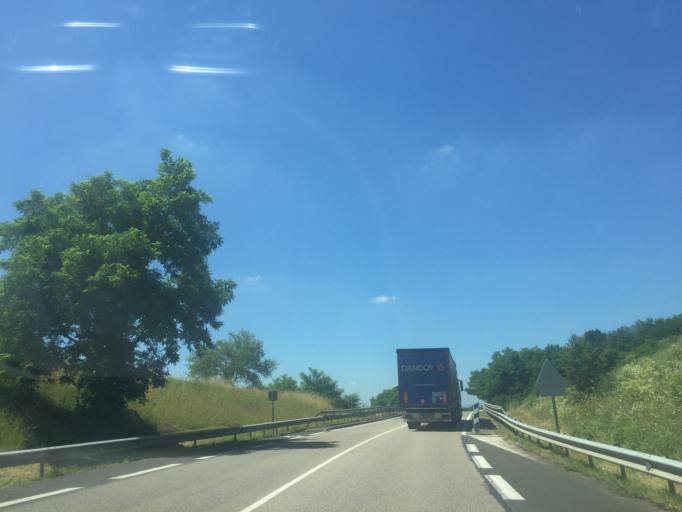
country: FR
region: Rhone-Alpes
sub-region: Departement du Rhone
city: Pusignan
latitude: 45.7428
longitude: 5.0801
